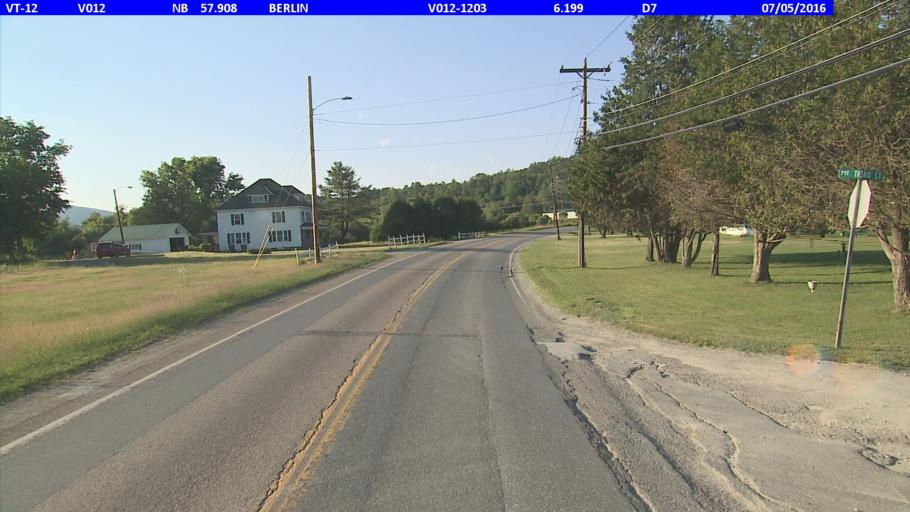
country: US
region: Vermont
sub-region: Washington County
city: Montpelier
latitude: 44.2422
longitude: -72.5948
